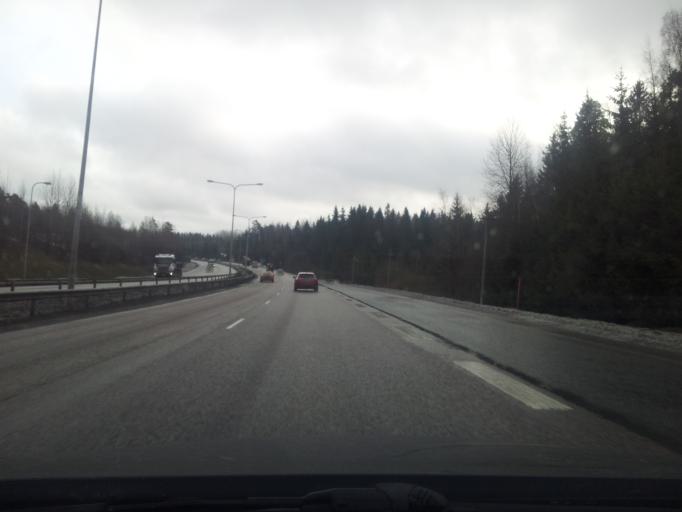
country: FI
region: Uusimaa
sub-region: Helsinki
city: Kauniainen
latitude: 60.2036
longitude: 24.6992
